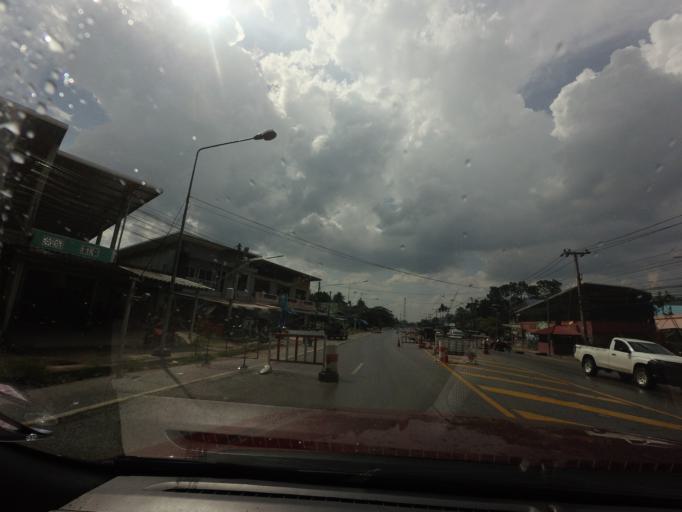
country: TH
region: Yala
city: Krong Pi Nang
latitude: 6.4147
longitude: 101.2798
